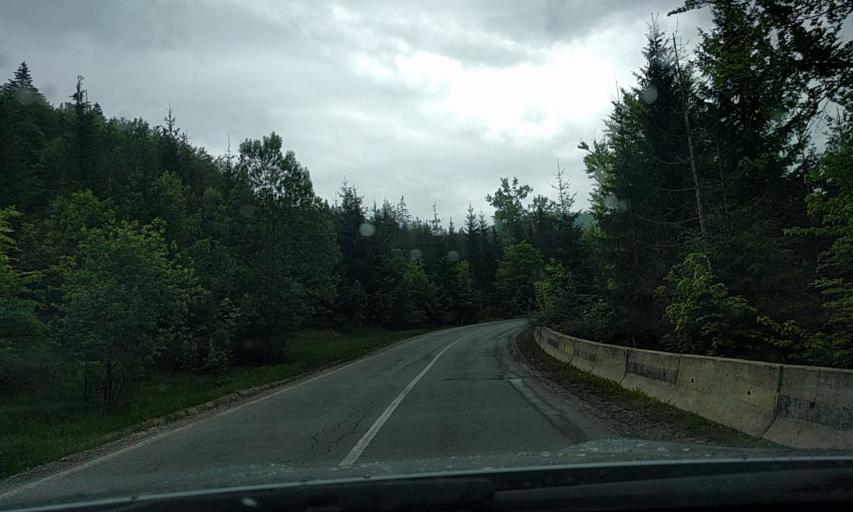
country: RO
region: Prahova
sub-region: Oras Sinaia
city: Sinaia
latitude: 45.3006
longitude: 25.5195
